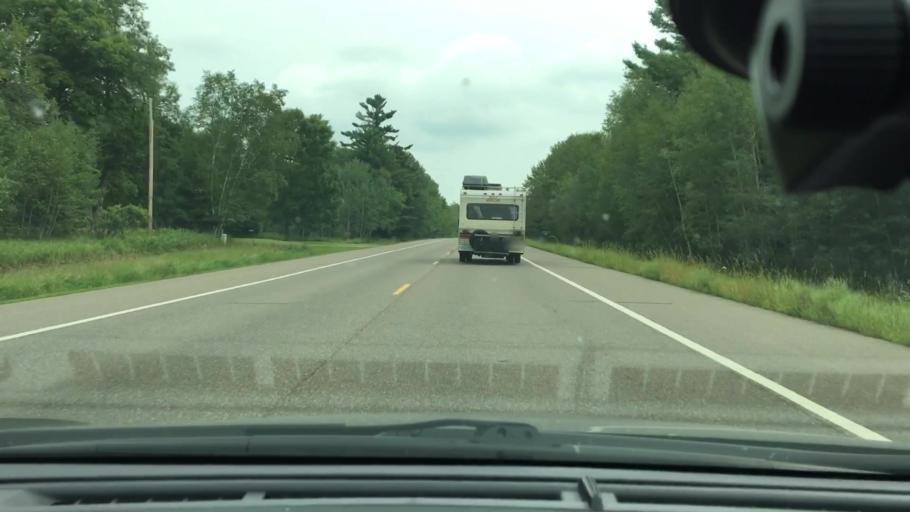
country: US
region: Minnesota
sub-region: Crow Wing County
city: Crosby
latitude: 46.4105
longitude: -93.8533
